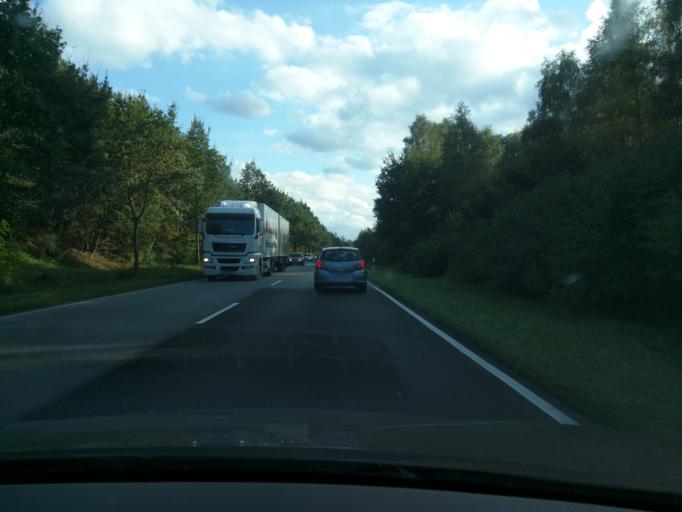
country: DE
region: Schleswig-Holstein
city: Escheburg
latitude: 53.4435
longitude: 10.3372
